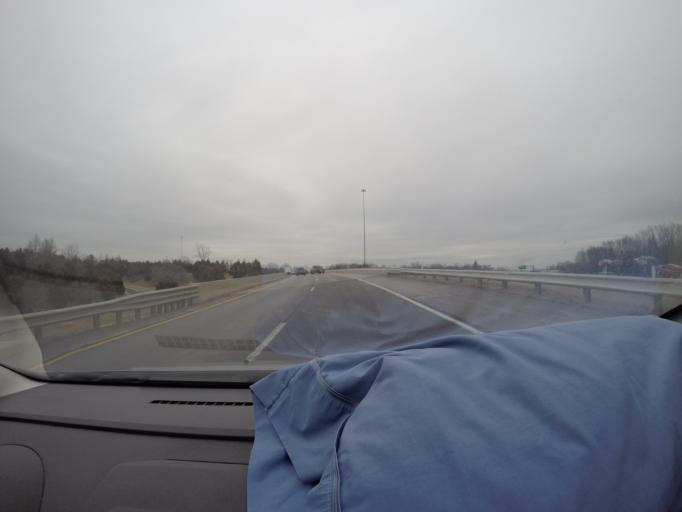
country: US
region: Missouri
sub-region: Saint Charles County
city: Wentzville
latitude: 38.8042
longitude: -90.8329
